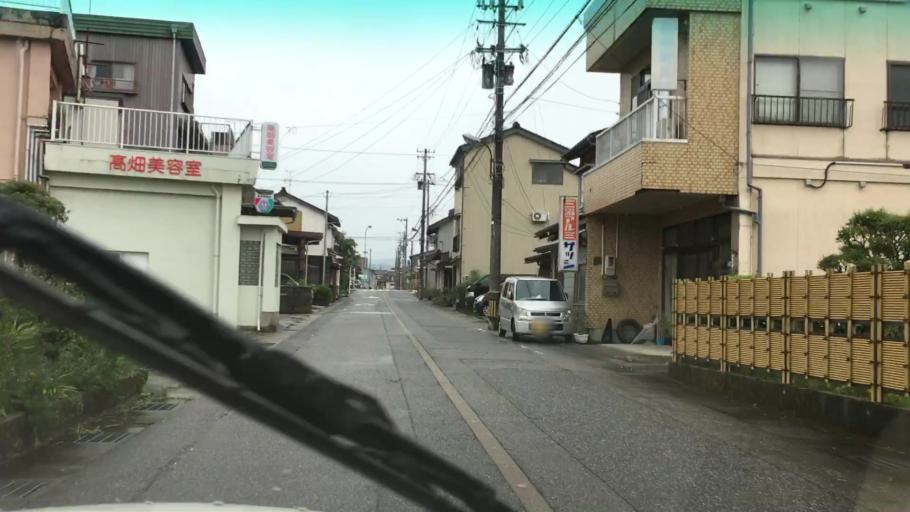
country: JP
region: Toyama
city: Kamiichi
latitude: 36.6628
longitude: 137.3162
